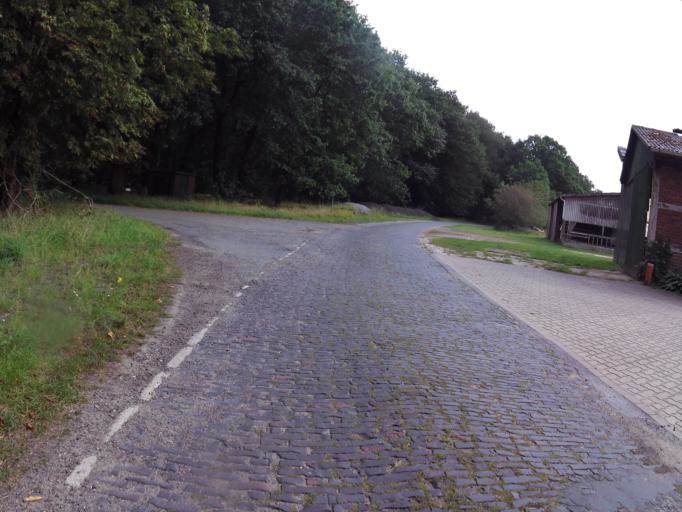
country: DE
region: Lower Saxony
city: Kohlen
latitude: 53.5046
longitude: 8.9127
